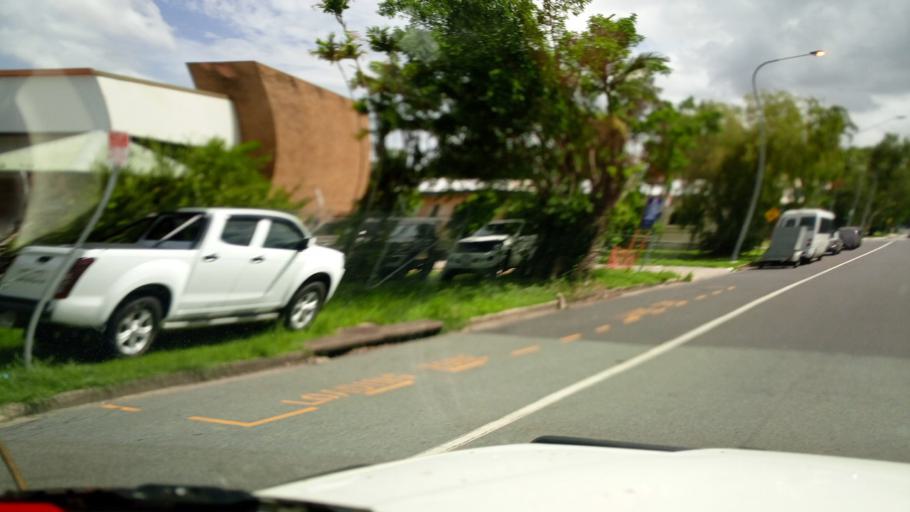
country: AU
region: Queensland
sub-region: Cairns
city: Woree
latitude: -16.9428
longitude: 145.7429
